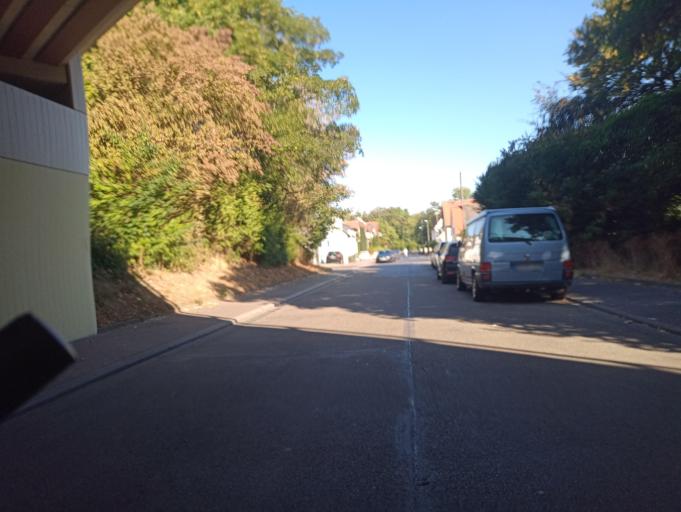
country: DE
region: Hesse
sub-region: Regierungsbezirk Darmstadt
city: Bad Homburg vor der Hoehe
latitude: 50.2189
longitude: 8.6297
